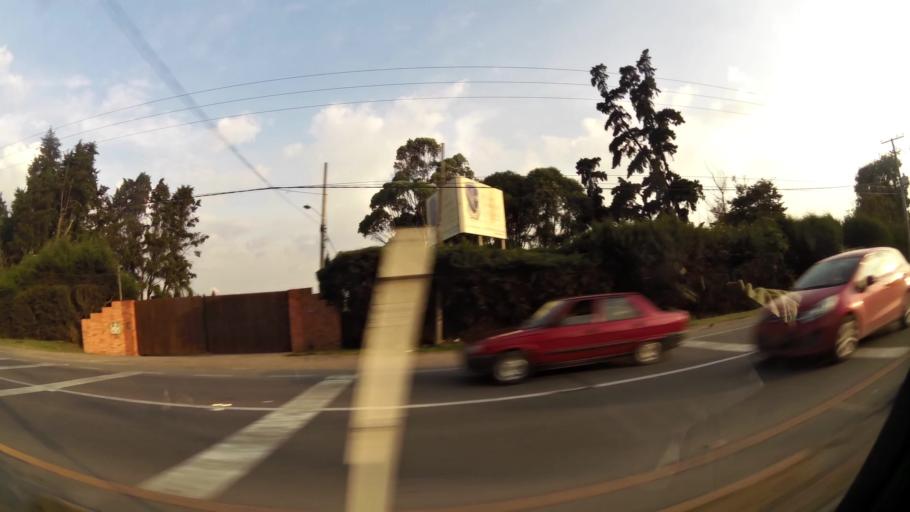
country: CO
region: Cundinamarca
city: Cota
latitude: 4.7831
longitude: -74.1300
